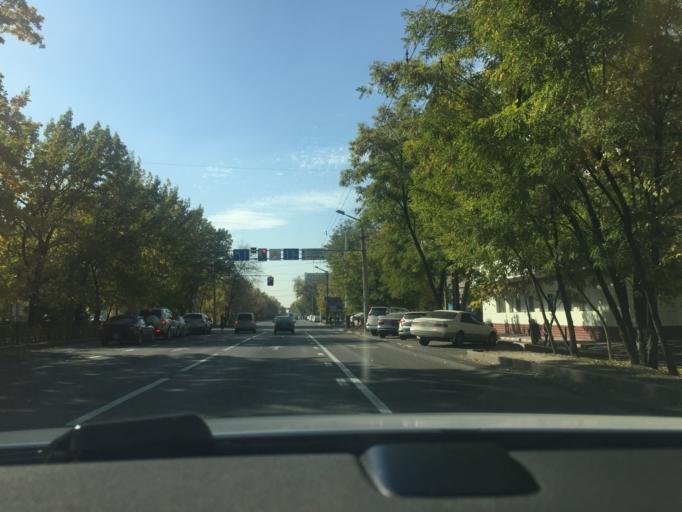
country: KZ
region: Almaty Qalasy
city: Almaty
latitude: 43.2395
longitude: 76.9004
